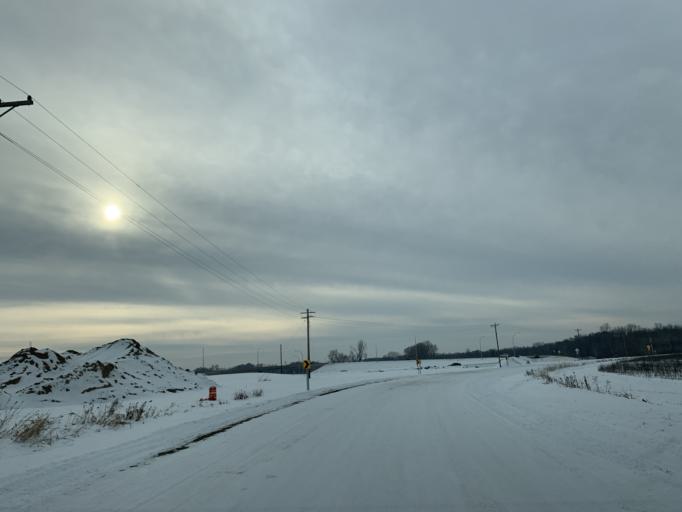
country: US
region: Minnesota
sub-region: Washington County
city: Forest Lake
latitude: 45.2926
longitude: -93.0039
